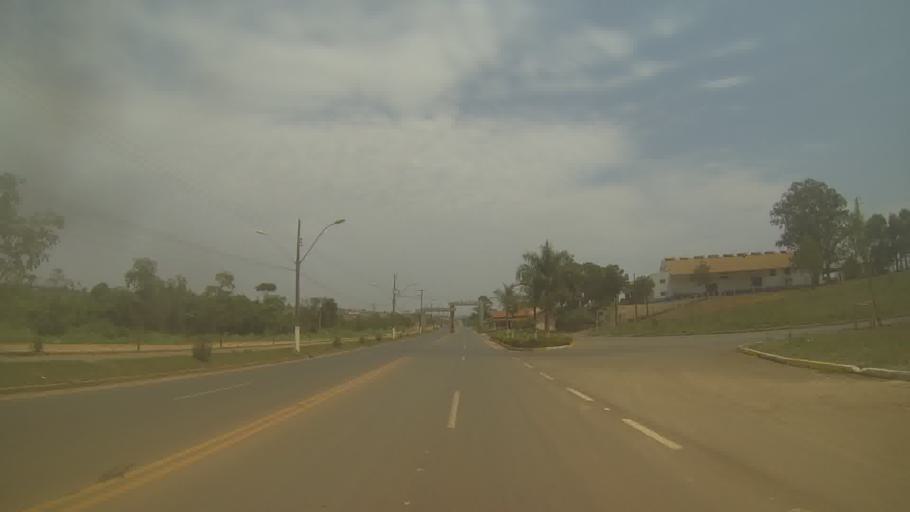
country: BR
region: Minas Gerais
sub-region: Bambui
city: Bambui
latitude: -20.0139
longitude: -45.9503
